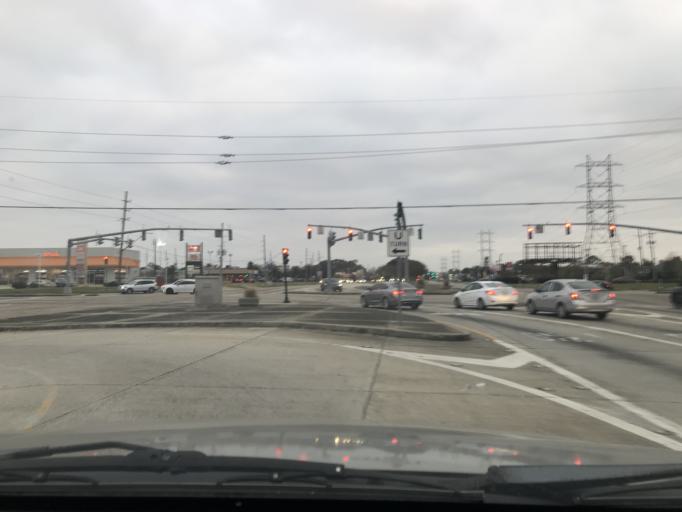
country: US
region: Louisiana
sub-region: Jefferson Parish
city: Marrero
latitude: 29.8753
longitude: -90.0976
